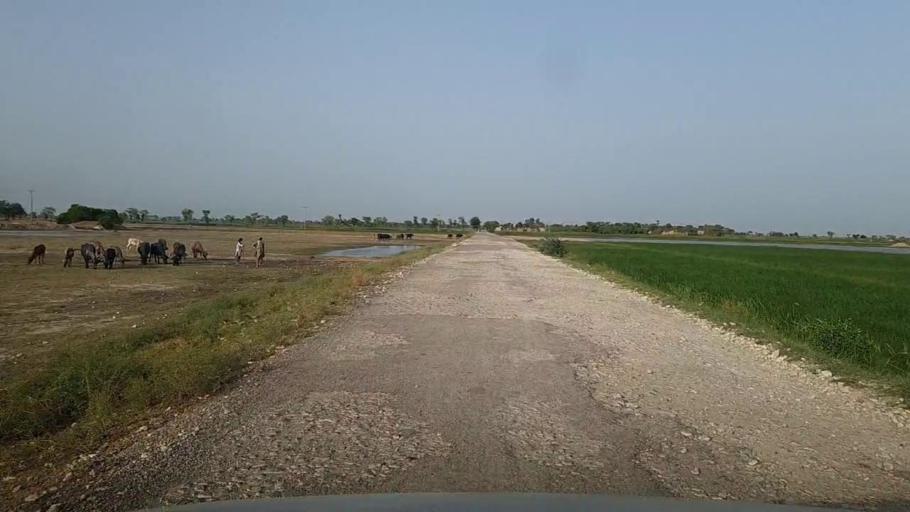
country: PK
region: Sindh
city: Khairpur Nathan Shah
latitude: 27.1572
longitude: 67.7474
